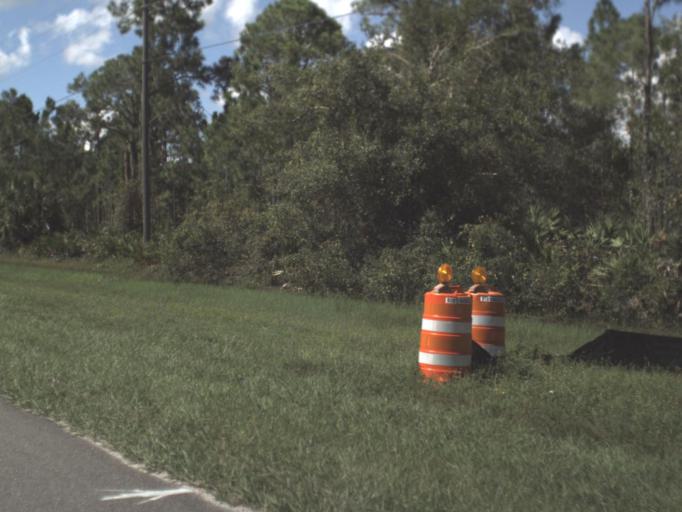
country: US
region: Florida
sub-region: Sarasota County
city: The Meadows
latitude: 27.4101
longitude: -82.3356
